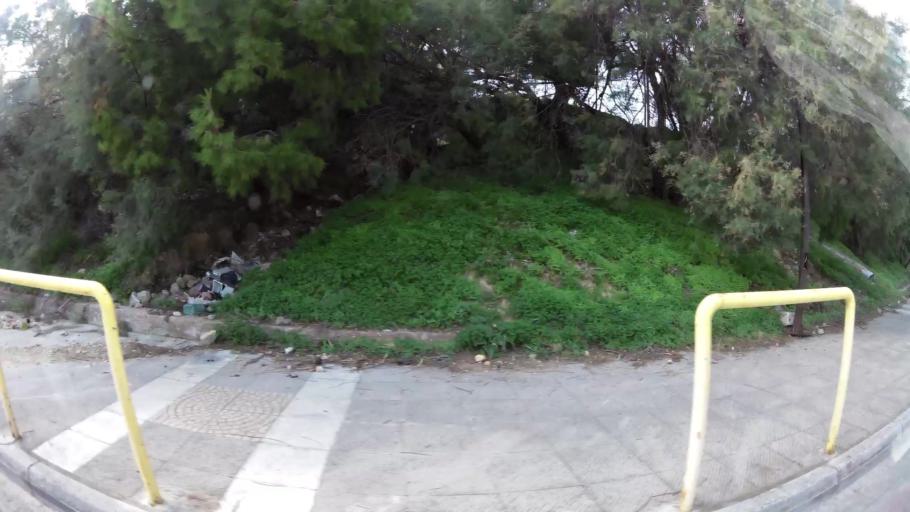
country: GR
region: Attica
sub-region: Nomarchia Athinas
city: Petroupolis
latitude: 38.0296
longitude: 23.6737
